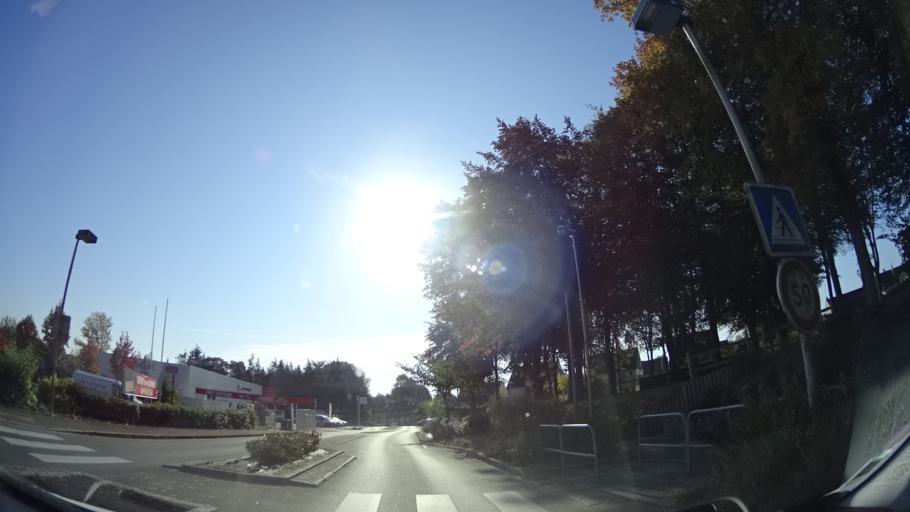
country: FR
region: Brittany
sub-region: Departement d'Ille-et-Vilaine
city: Geveze
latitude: 48.2197
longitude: -1.7860
